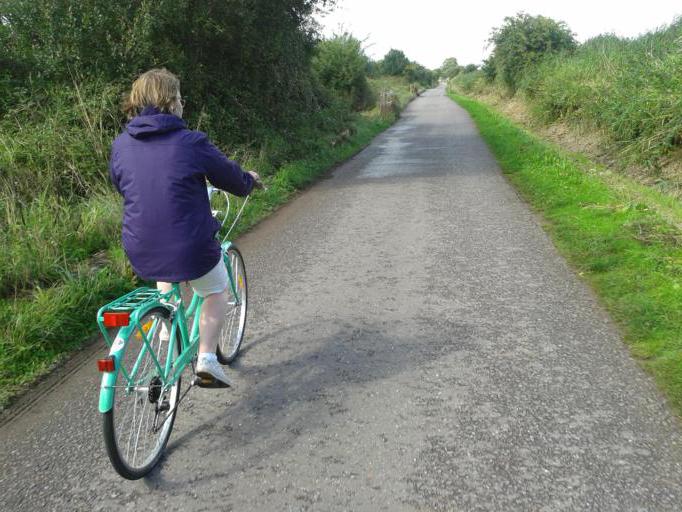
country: GB
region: England
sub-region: Devon
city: Topsham
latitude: 50.6684
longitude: -3.4687
